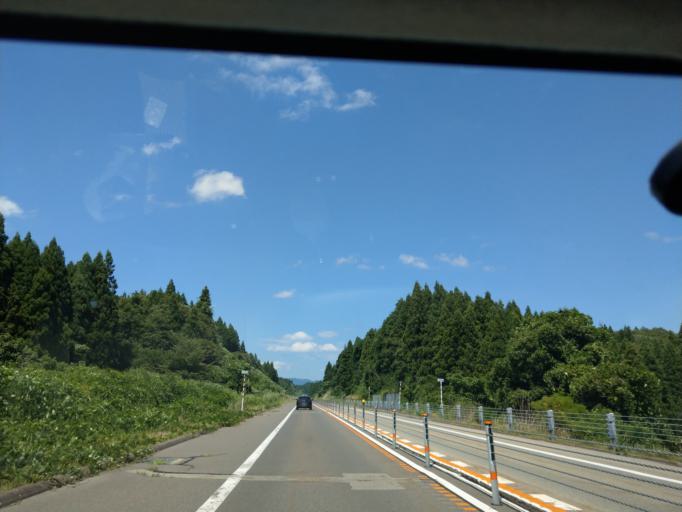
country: JP
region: Akita
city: Akita
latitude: 39.6871
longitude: 140.1857
